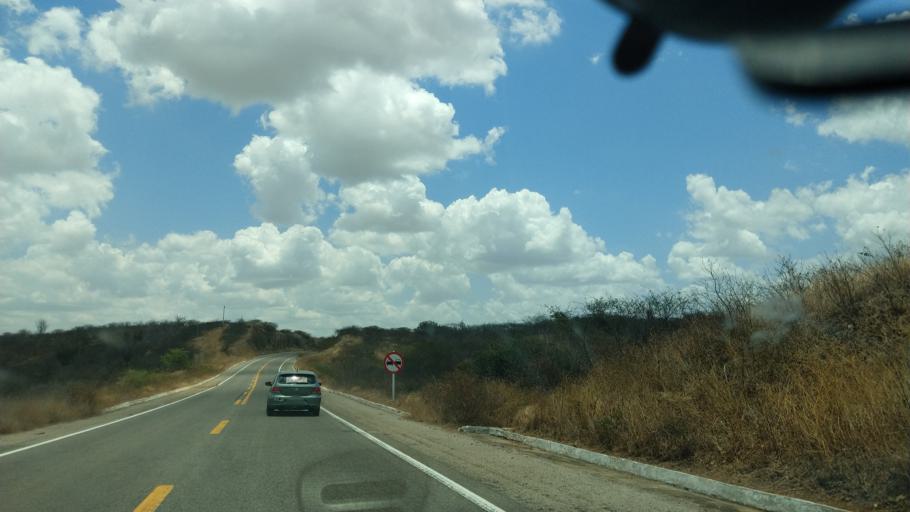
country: BR
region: Rio Grande do Norte
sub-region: Cerro Cora
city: Cerro Cora
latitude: -6.2106
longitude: -36.2995
